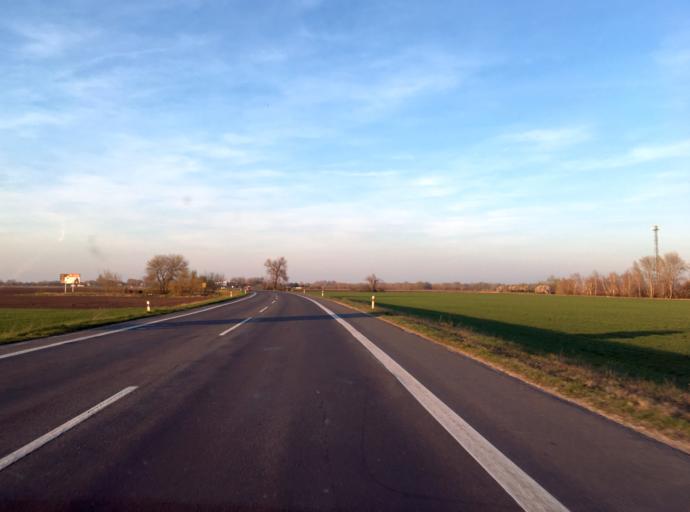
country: SK
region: Nitriansky
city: Komarno
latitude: 47.7973
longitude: 18.1821
